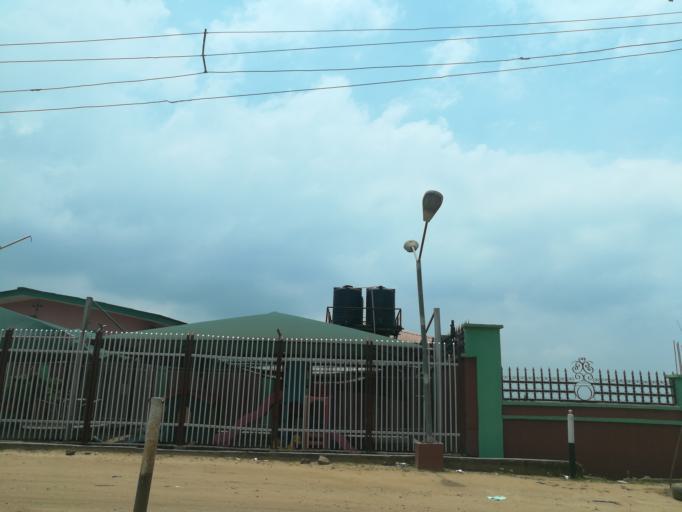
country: NG
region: Lagos
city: Ikorodu
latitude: 6.6255
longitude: 3.5517
